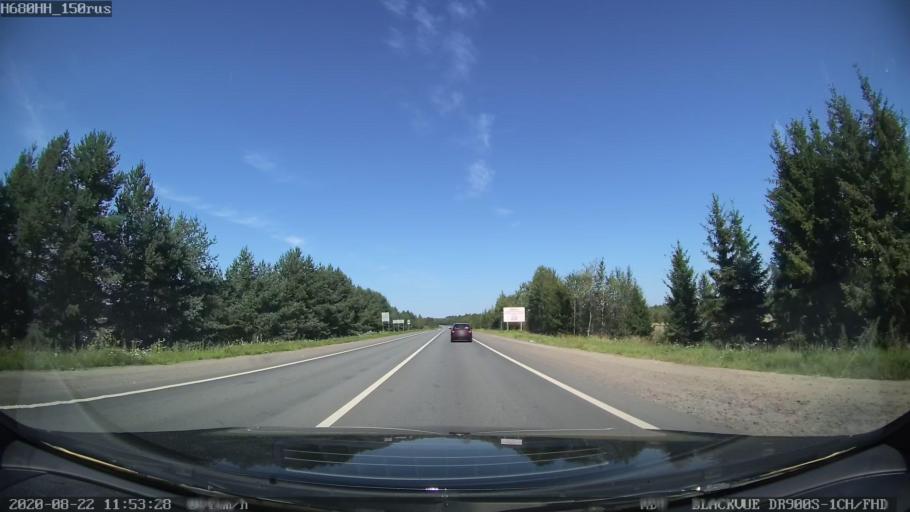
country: RU
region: Tverskaya
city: Vasil'yevskiy Mokh
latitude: 57.1274
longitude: 36.1110
